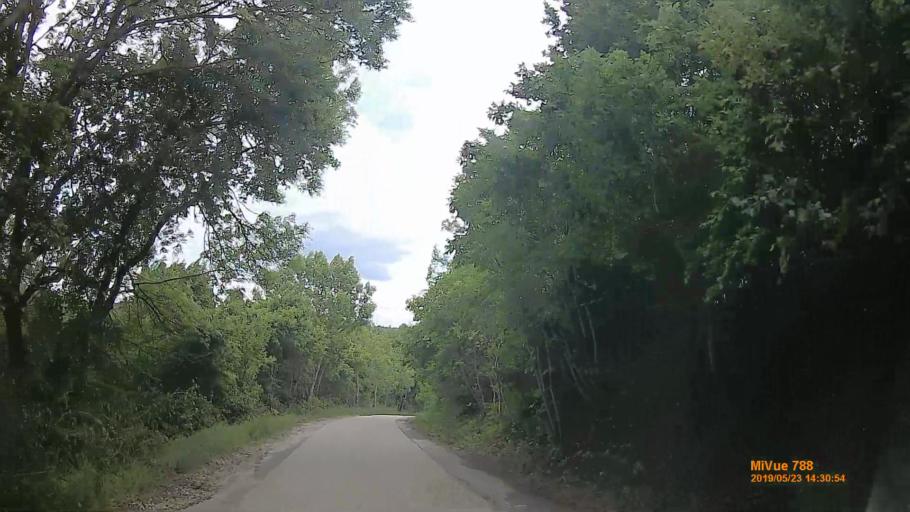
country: HU
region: Veszprem
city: Nemesvamos
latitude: 47.1049
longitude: 17.8602
